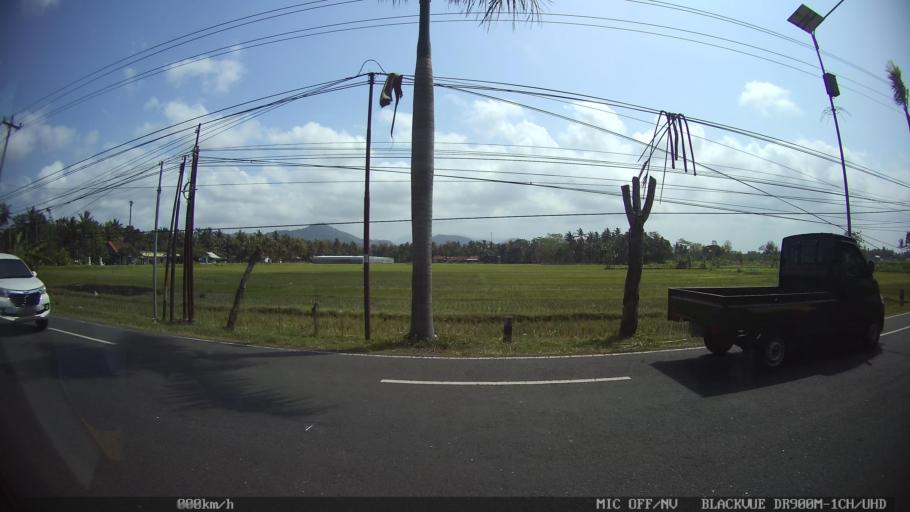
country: ID
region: Daerah Istimewa Yogyakarta
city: Srandakan
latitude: -7.8903
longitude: 110.1099
